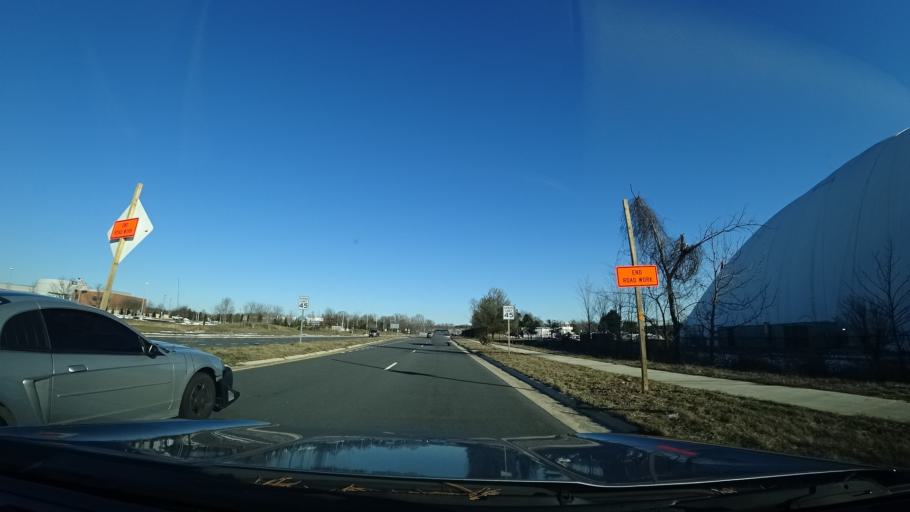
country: US
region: Virginia
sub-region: Loudoun County
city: Sterling
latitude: 39.0280
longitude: -77.4465
